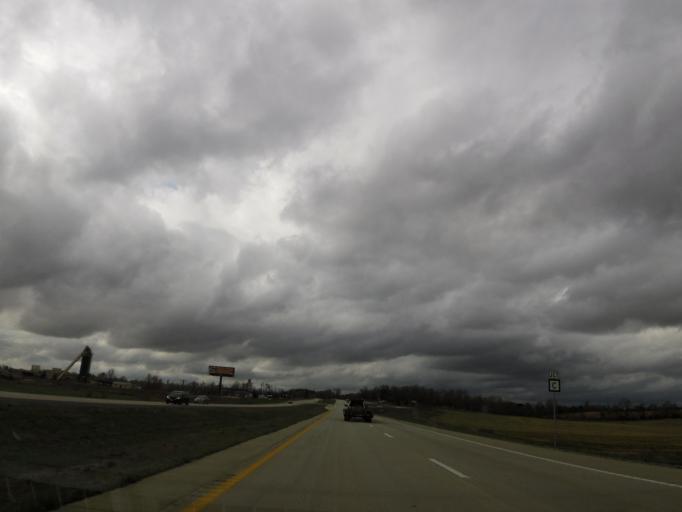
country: US
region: Missouri
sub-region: Butler County
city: Poplar Bluff
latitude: 36.6900
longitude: -90.4826
